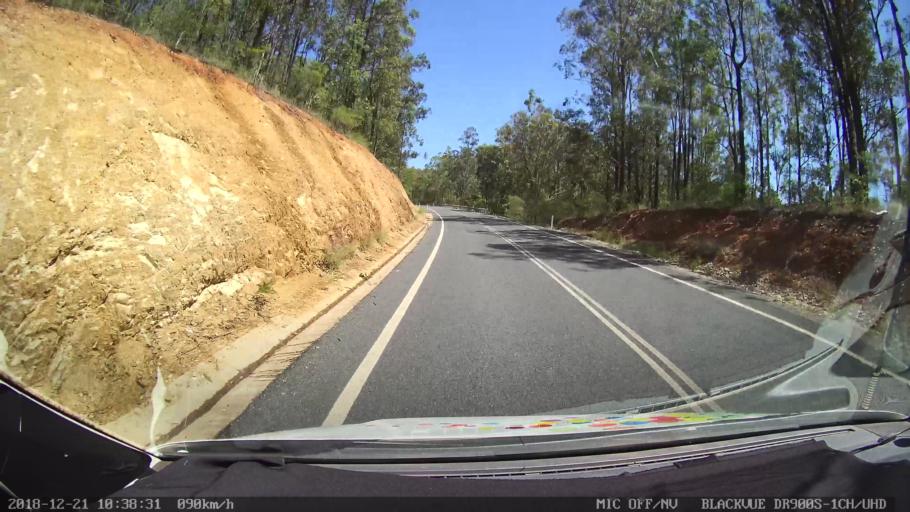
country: AU
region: New South Wales
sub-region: Clarence Valley
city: South Grafton
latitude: -29.6145
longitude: 152.6082
